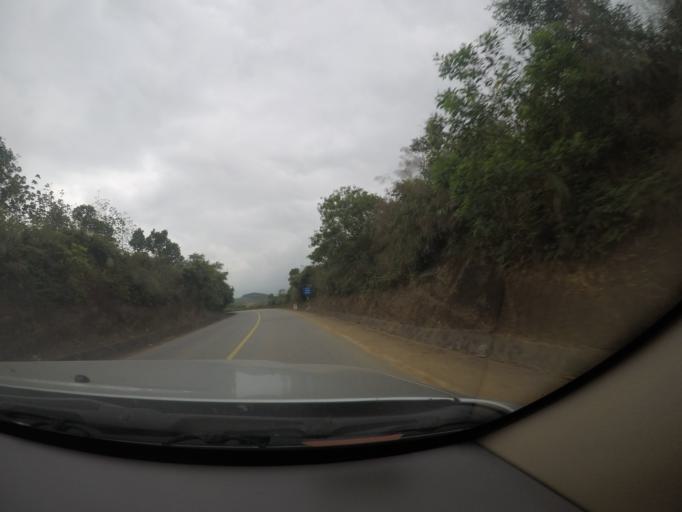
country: VN
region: Quang Binh
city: Hoan Lao
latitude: 17.6077
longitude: 106.4065
